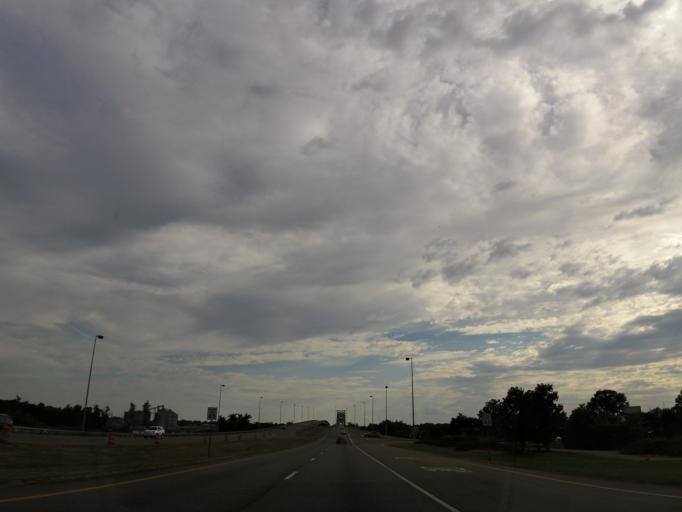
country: US
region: Alabama
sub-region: Morgan County
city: Decatur
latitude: 34.6178
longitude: -86.9679
